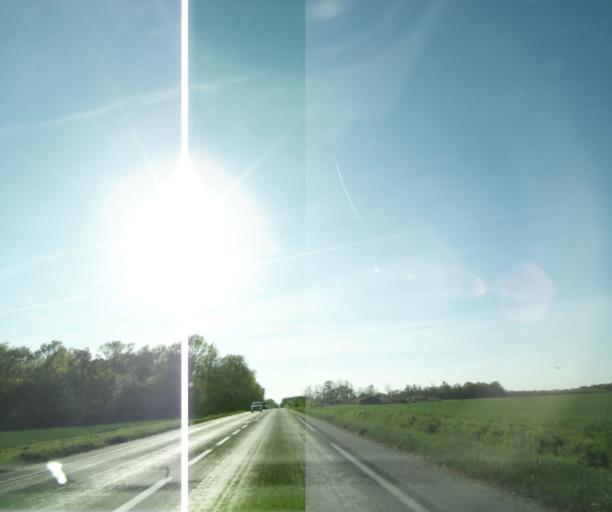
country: FR
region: Ile-de-France
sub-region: Departement de Seine-et-Marne
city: Bailly-Carrois
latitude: 48.5563
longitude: 2.9723
